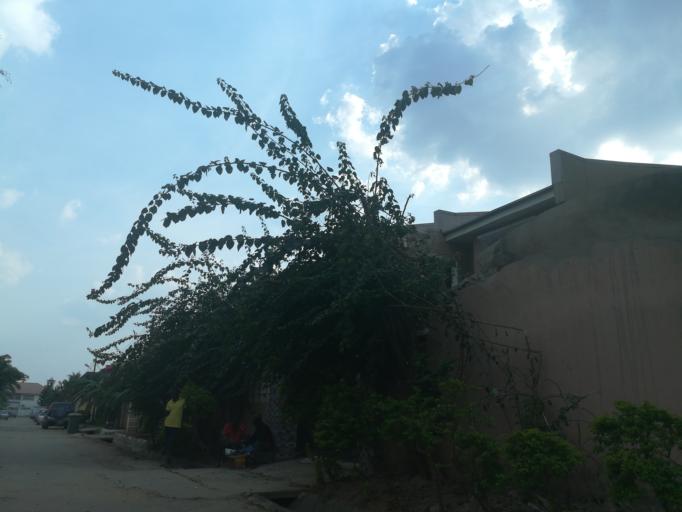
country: NG
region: Abuja Federal Capital Territory
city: Abuja
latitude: 9.0856
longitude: 7.4144
